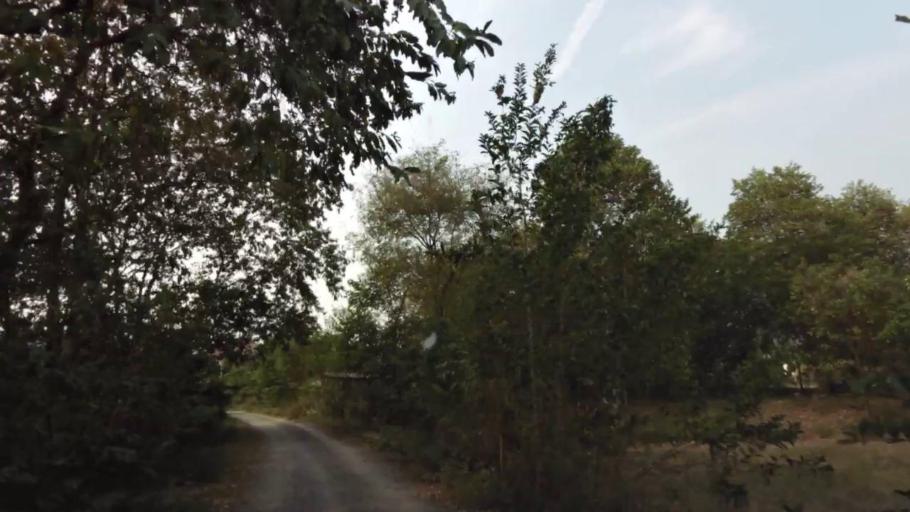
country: TH
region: Phra Nakhon Si Ayutthaya
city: Phra Nakhon Si Ayutthaya
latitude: 14.3422
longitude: 100.5673
